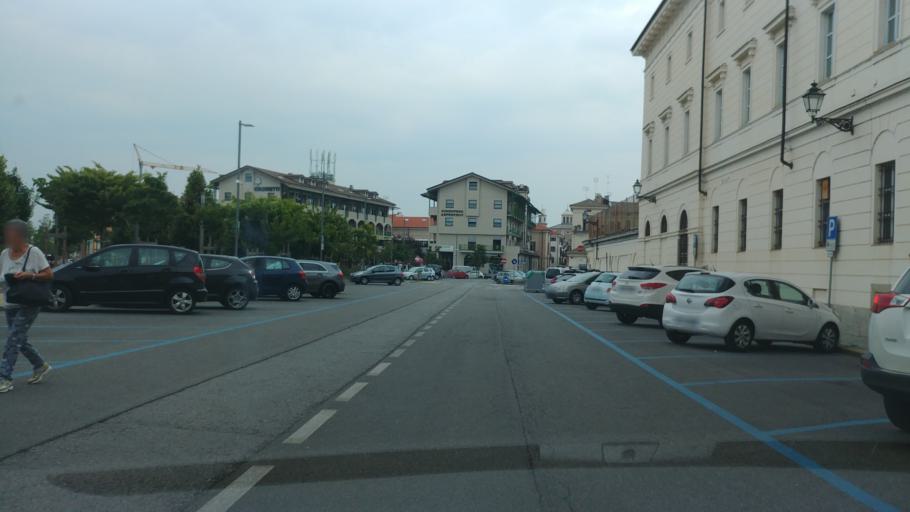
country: IT
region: Piedmont
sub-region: Provincia di Cuneo
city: Cuneo
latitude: 44.3914
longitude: 7.5464
